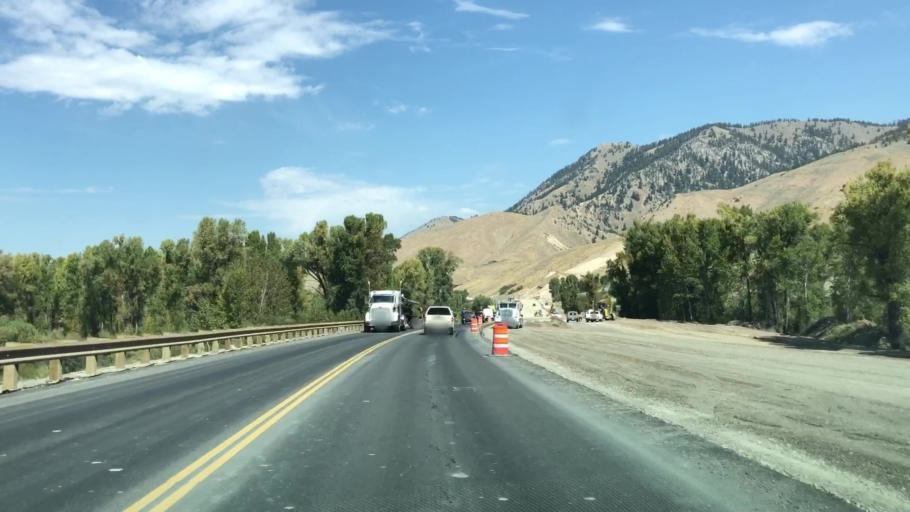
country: US
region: Wyoming
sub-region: Teton County
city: South Park
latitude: 43.3864
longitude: -110.7464
